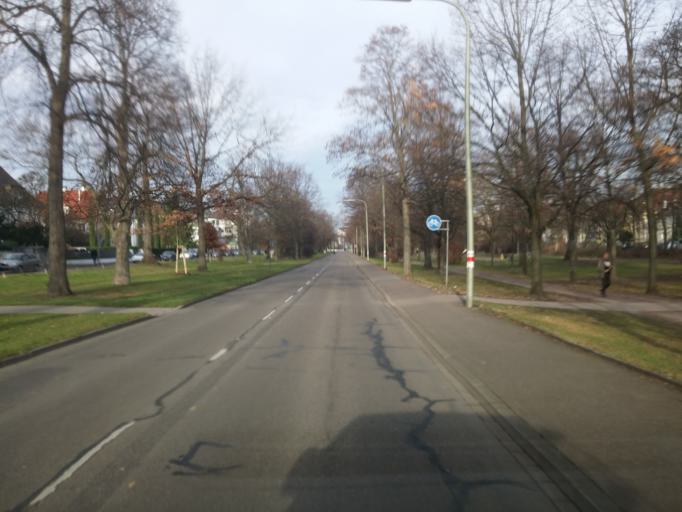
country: DE
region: Baden-Wuerttemberg
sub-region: Karlsruhe Region
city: Karlsruhe
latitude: 48.9957
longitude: 8.3963
